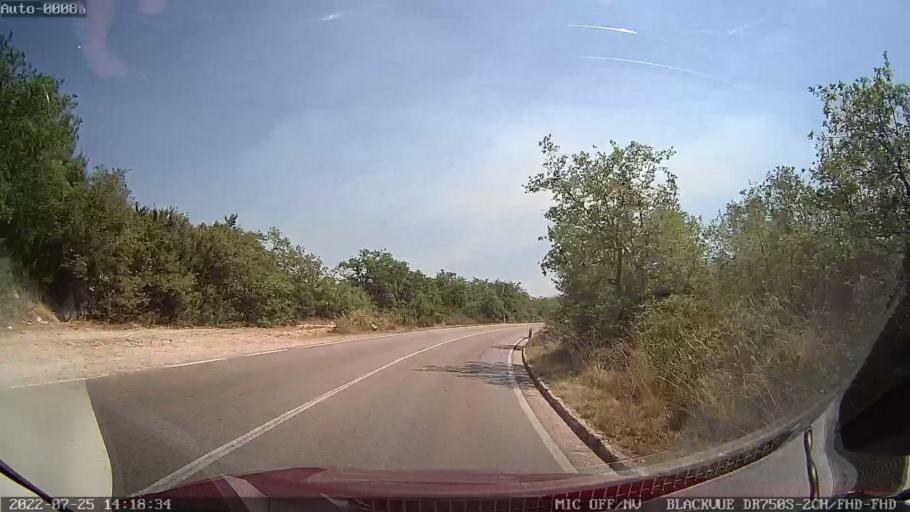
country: HR
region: Zadarska
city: Zadar
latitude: 44.1827
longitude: 15.2807
